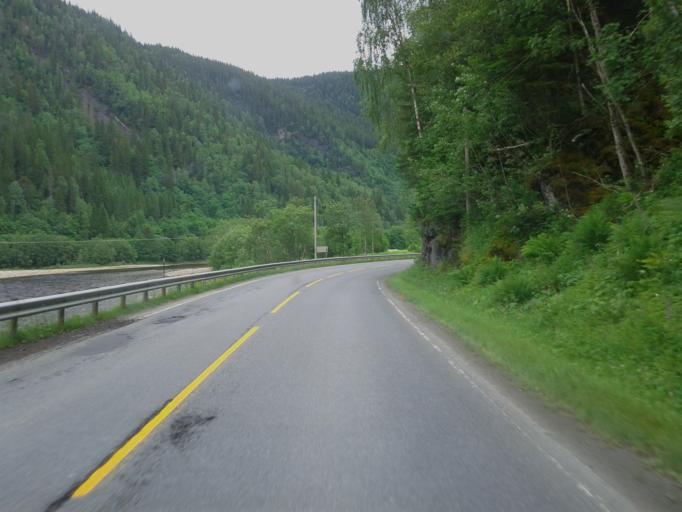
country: NO
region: Sor-Trondelag
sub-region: Midtre Gauldal
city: Storen
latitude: 62.9908
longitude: 10.5246
